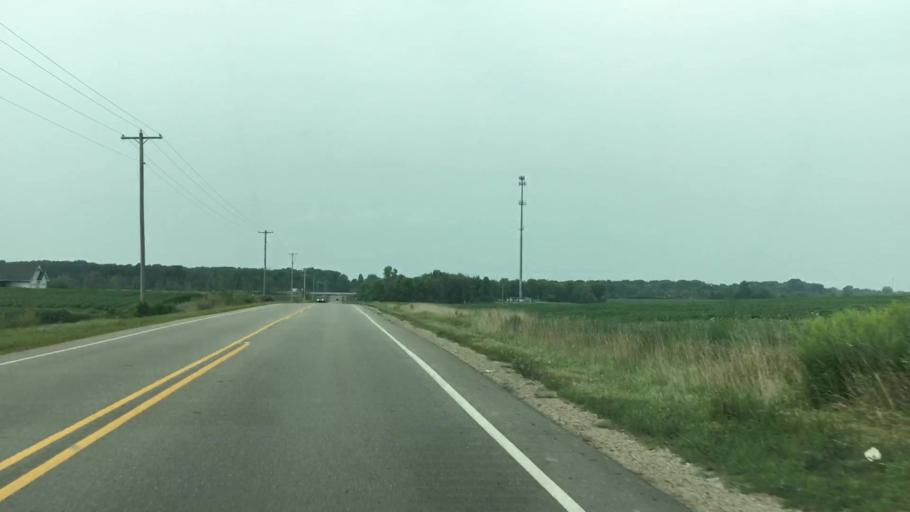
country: US
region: Michigan
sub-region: Ottawa County
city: Hudsonville
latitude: 42.8293
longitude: -85.9006
